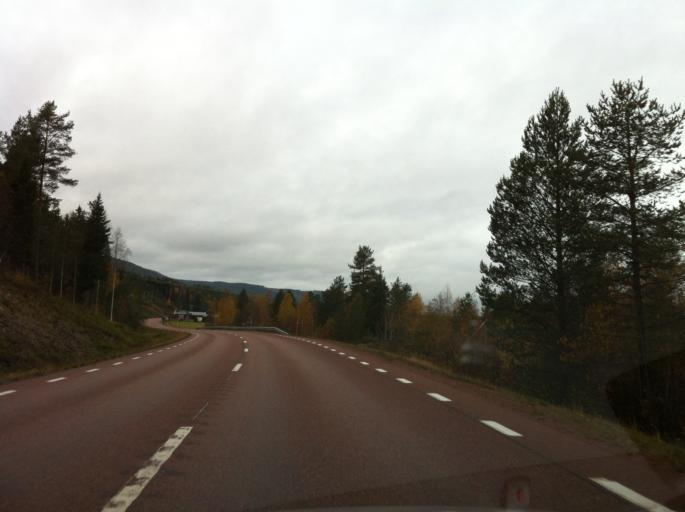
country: SE
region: Dalarna
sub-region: Alvdalens Kommun
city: AElvdalen
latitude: 61.2710
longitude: 13.8021
